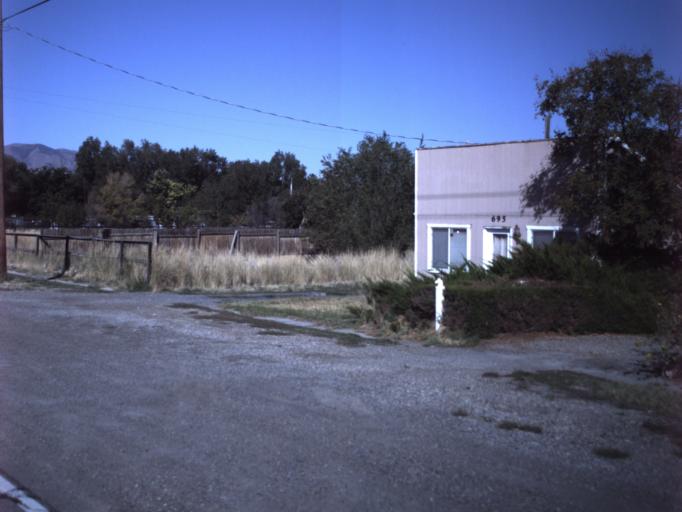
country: US
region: Utah
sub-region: Tooele County
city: Grantsville
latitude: 40.5997
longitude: -112.4325
